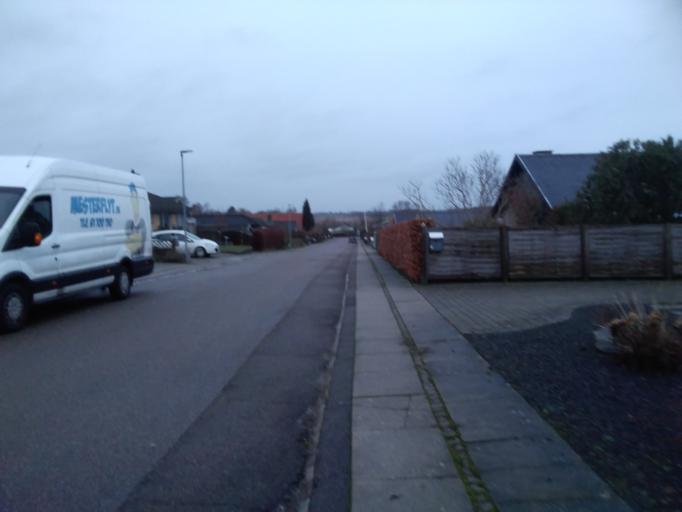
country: DK
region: Capital Region
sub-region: Egedal Kommune
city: Olstykke
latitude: 55.7865
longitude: 12.1345
